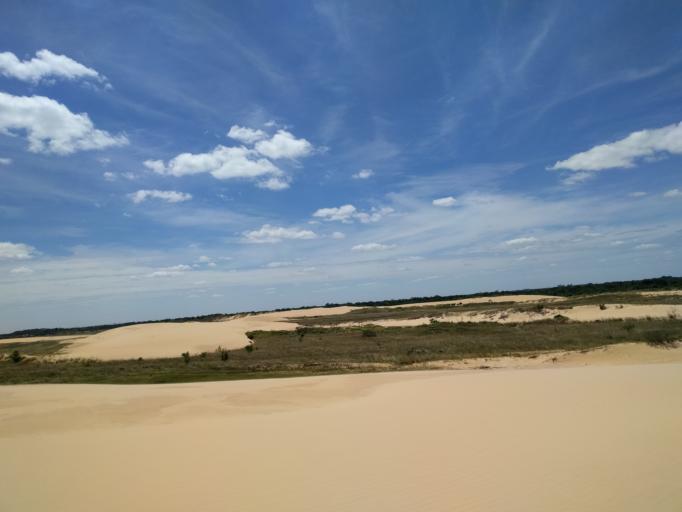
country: BO
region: Santa Cruz
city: Santa Cruz de la Sierra
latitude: -17.9519
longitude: -63.1517
